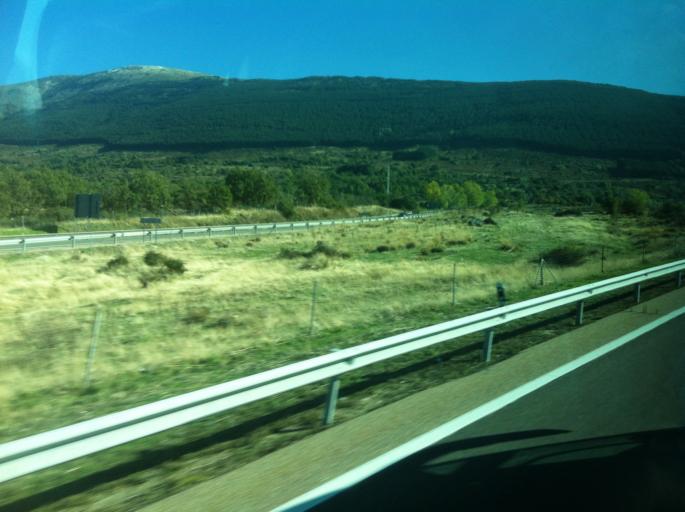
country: ES
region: Castille and Leon
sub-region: Provincia de Segovia
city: Cerezo de Abajo
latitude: 41.1783
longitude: -3.5830
